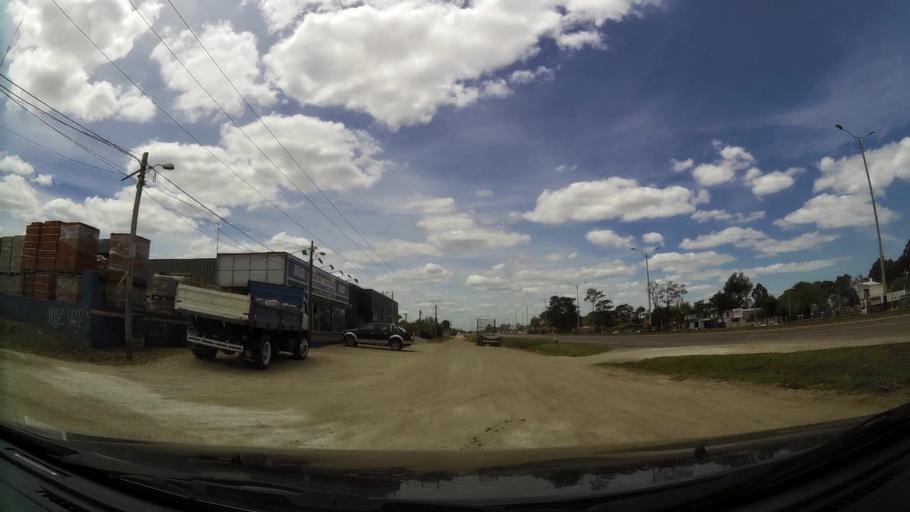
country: UY
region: Canelones
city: Pando
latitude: -34.8087
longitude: -55.9352
